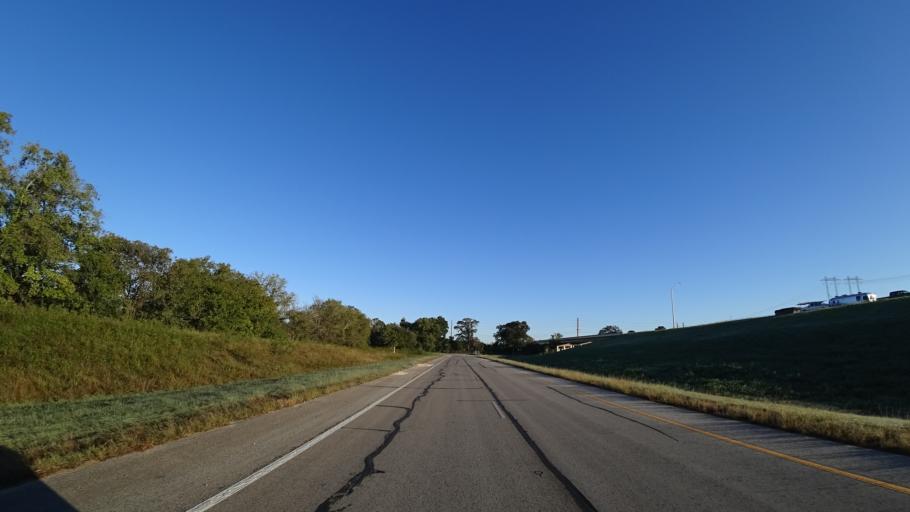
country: US
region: Texas
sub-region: Travis County
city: Hornsby Bend
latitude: 30.2076
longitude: -97.6235
